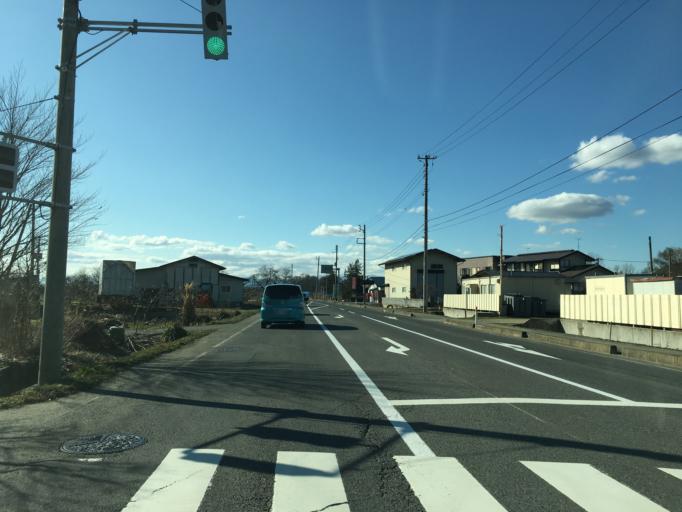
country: JP
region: Yamagata
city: Takahata
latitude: 38.0040
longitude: 140.1635
